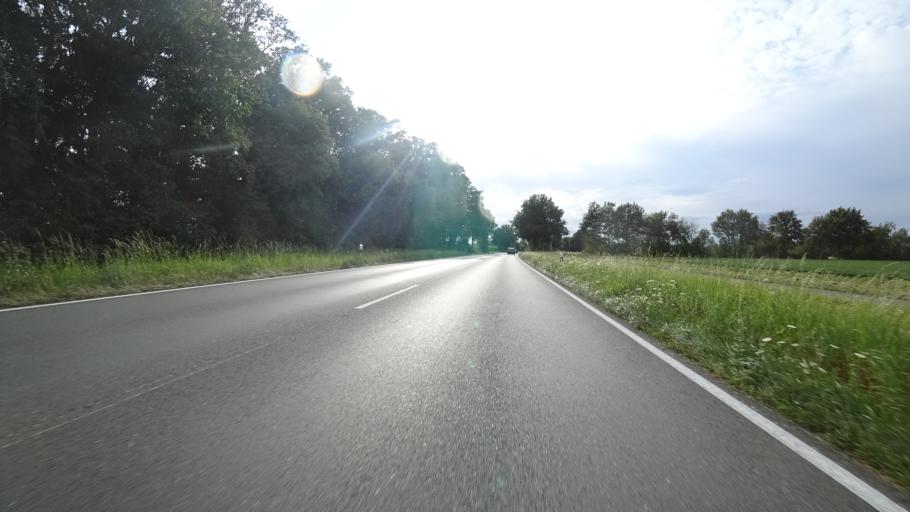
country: DE
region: North Rhine-Westphalia
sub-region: Regierungsbezirk Munster
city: Beelen
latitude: 51.9718
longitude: 8.1604
